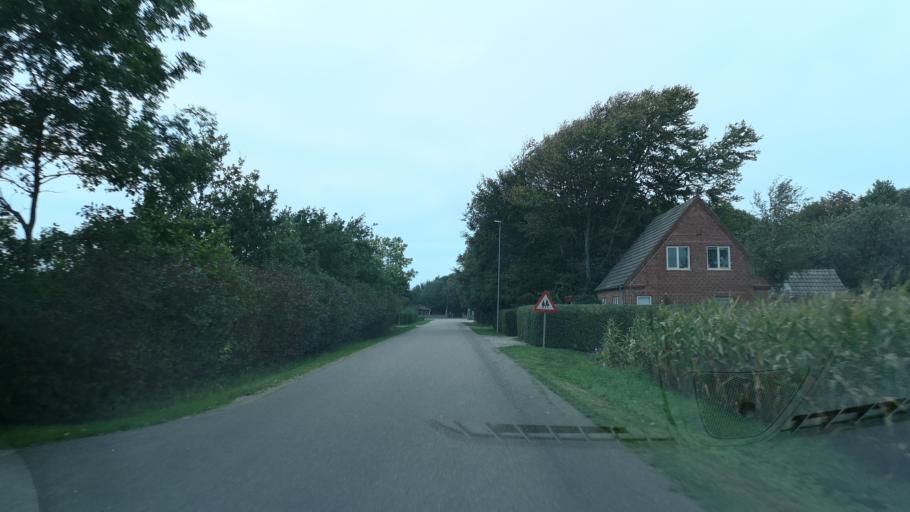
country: DK
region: Central Jutland
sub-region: Ringkobing-Skjern Kommune
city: Videbaek
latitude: 56.0671
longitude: 8.6089
